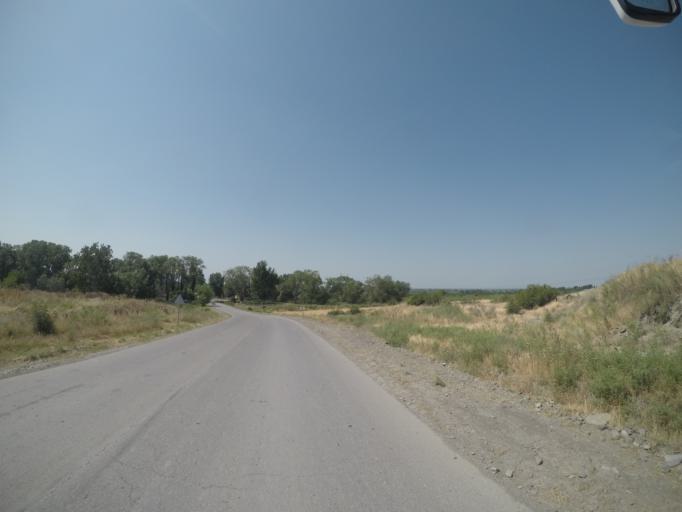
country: AZ
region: Agdas
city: Agdas
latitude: 40.7078
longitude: 47.5392
